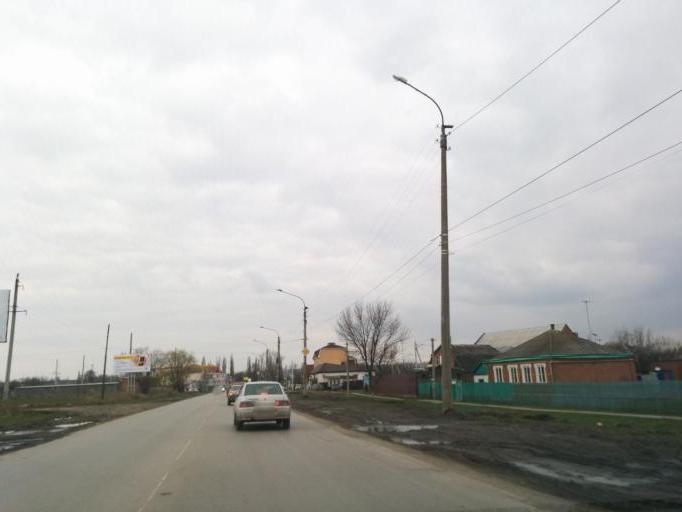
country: RU
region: Rostov
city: Novocherkassk
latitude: 47.4568
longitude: 40.1020
